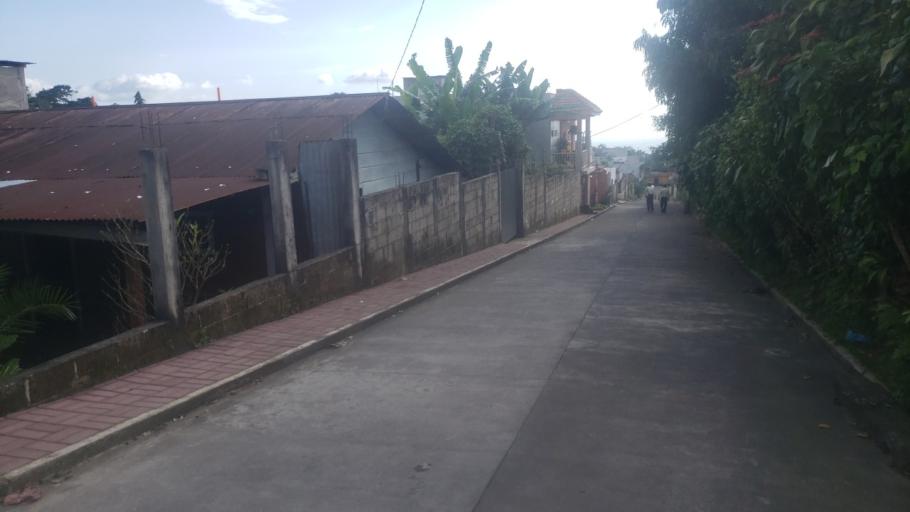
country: GT
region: Suchitepeque
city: Pueblo Nuevo
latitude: 14.6445
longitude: -91.5577
